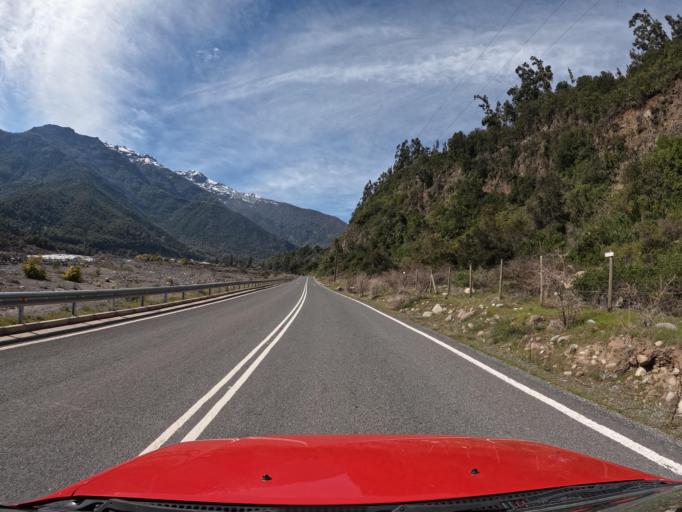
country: CL
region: Maule
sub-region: Provincia de Curico
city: Teno
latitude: -35.0035
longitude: -70.8268
